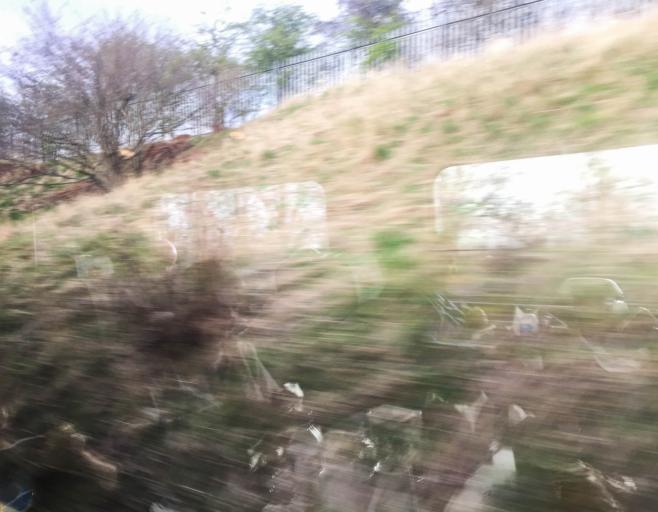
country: GB
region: Scotland
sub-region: South Lanarkshire
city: Carluke
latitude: 55.7348
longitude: -3.8554
